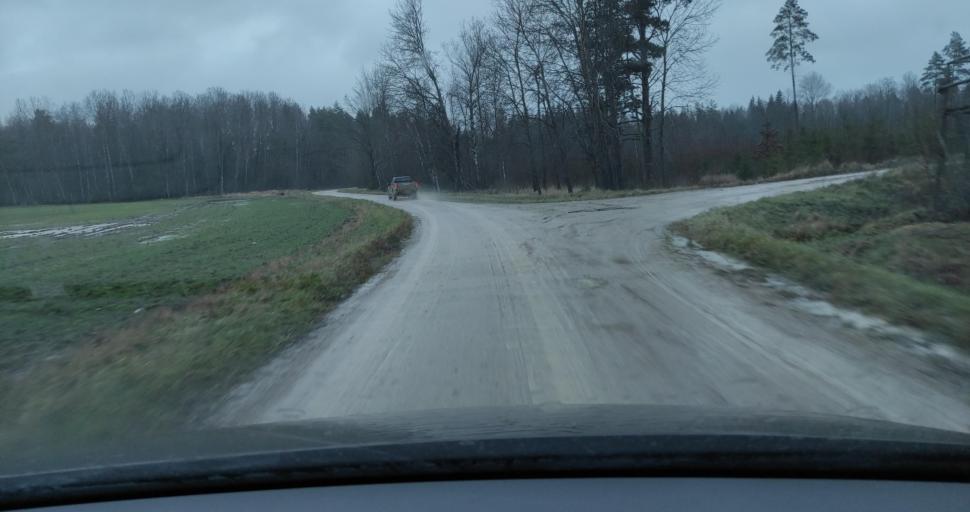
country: LV
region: Skrunda
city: Skrunda
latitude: 56.6030
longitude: 22.1217
